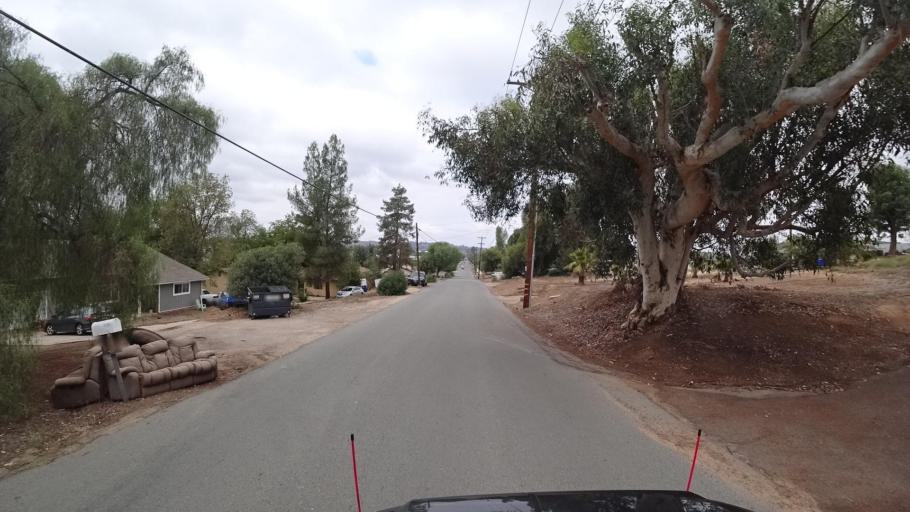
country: US
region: California
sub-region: San Diego County
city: Ramona
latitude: 33.0324
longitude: -116.8633
